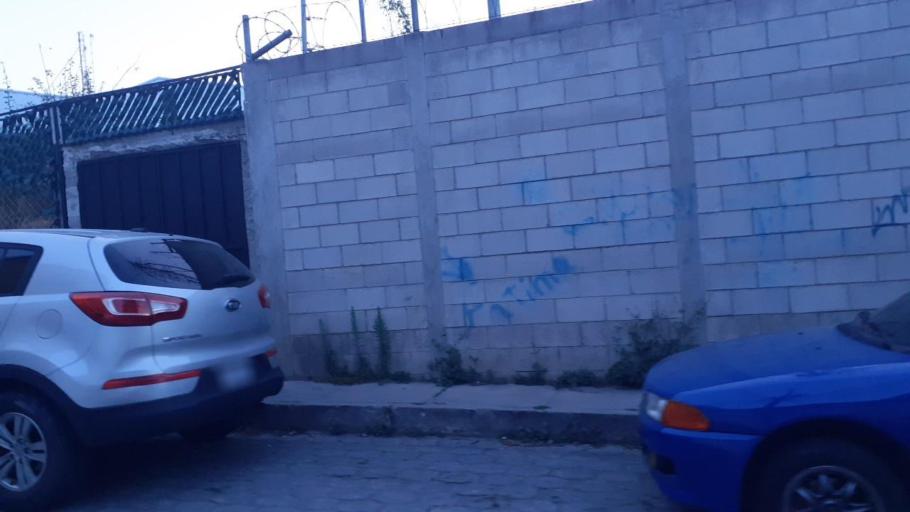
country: GT
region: Quetzaltenango
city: Quetzaltenango
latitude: 14.8311
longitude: -91.5236
